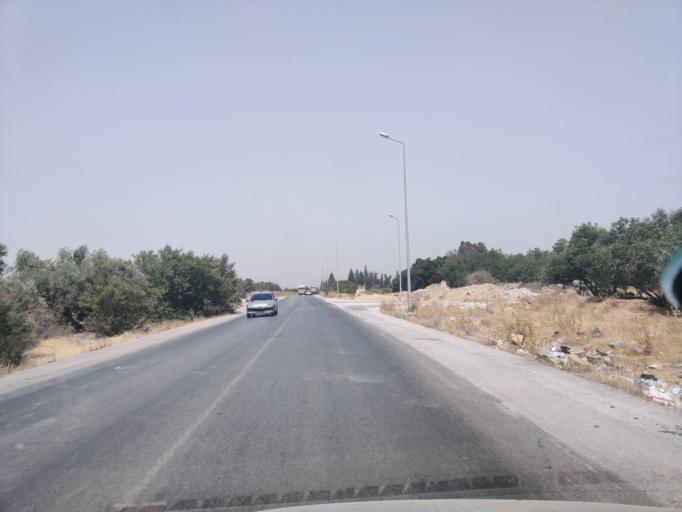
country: TN
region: Tunis
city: La Sebala du Mornag
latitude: 36.6737
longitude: 10.3185
